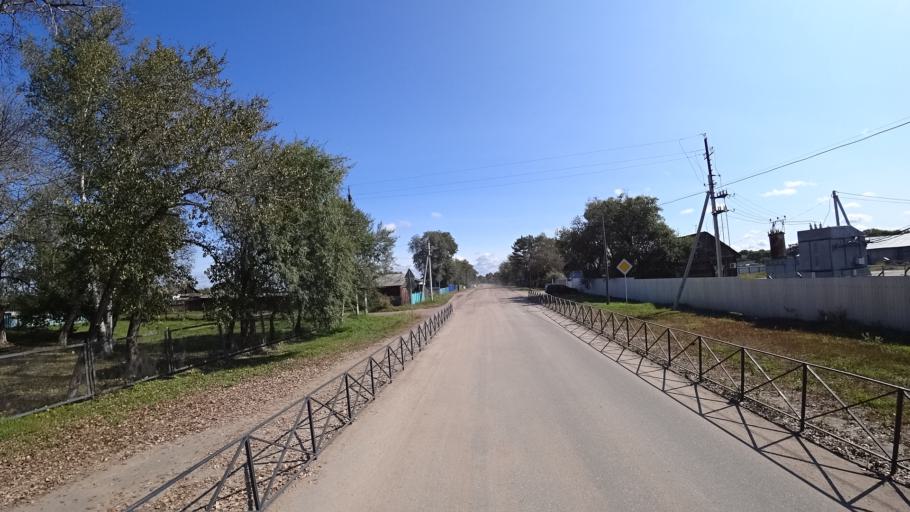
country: RU
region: Amur
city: Arkhara
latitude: 49.4028
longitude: 130.1405
